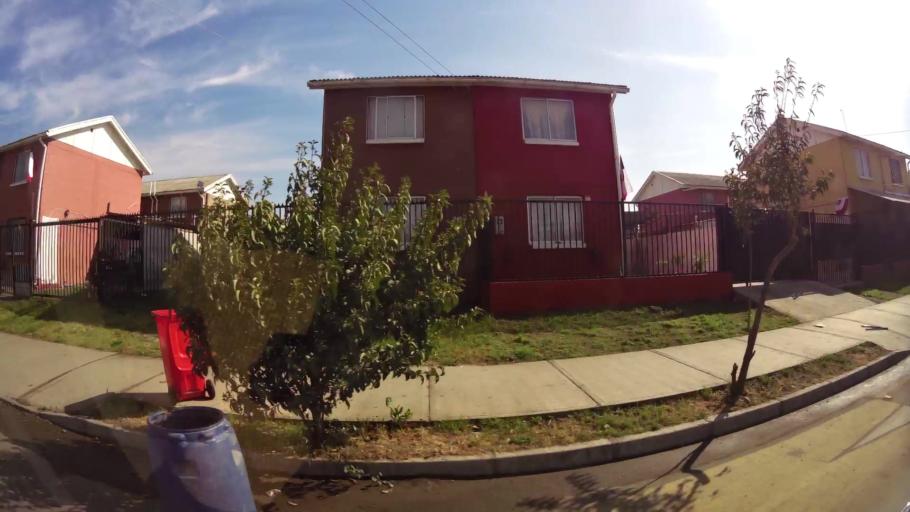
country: CL
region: Santiago Metropolitan
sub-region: Provincia de Talagante
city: El Monte
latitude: -33.6839
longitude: -70.9530
